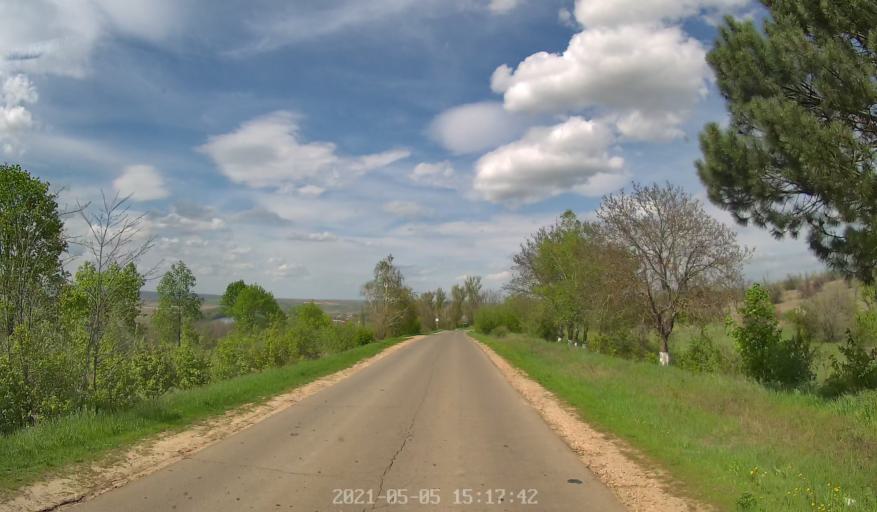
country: MD
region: Criuleni
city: Criuleni
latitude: 47.1141
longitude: 29.1944
